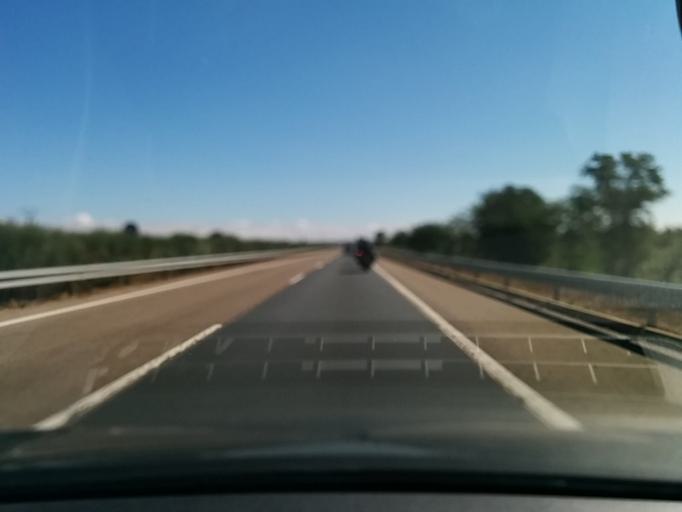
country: ES
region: Aragon
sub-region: Provincia de Huesca
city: Almudebar
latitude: 42.0273
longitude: -0.5967
